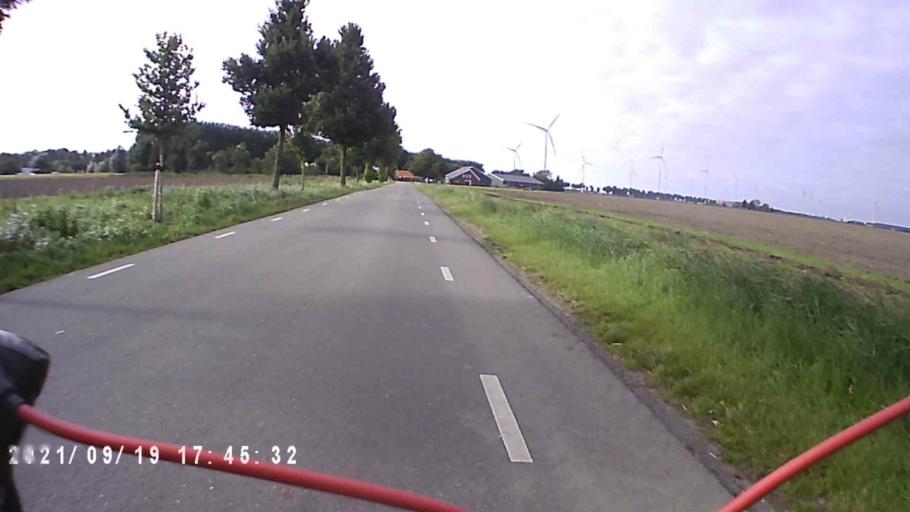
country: NL
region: Groningen
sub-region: Gemeente Delfzijl
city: Delfzijl
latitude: 53.2581
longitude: 6.9570
